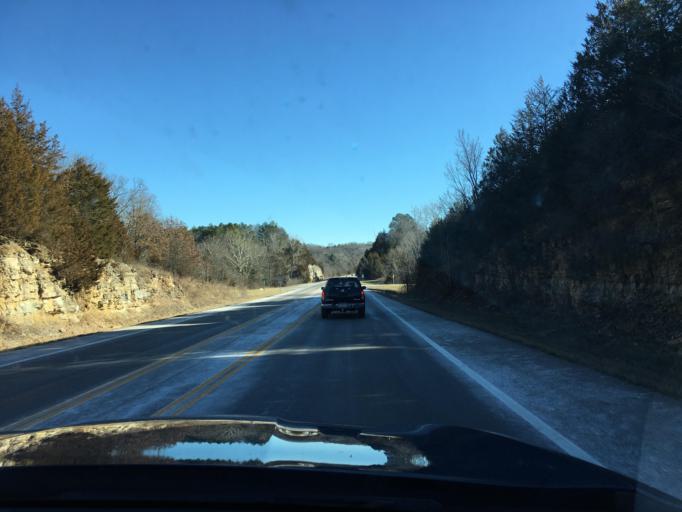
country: US
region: Missouri
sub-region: Jefferson County
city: De Soto
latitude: 38.1386
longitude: -90.4933
